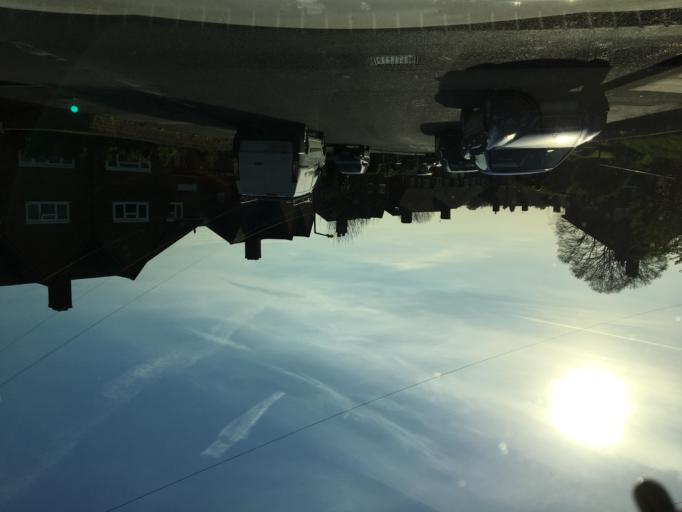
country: GB
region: England
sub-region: Greater London
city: Chislehurst
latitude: 51.4313
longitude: 0.0565
